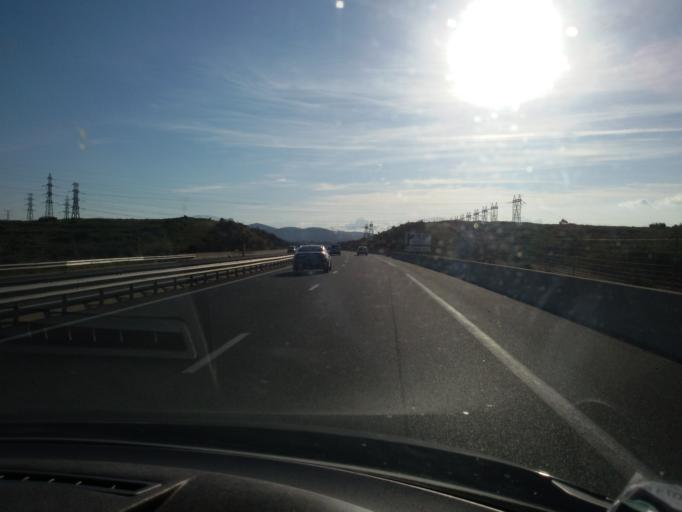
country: FR
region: Languedoc-Roussillon
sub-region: Departement de l'Herault
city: Murviel-les-Montpellier
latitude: 43.6326
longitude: 3.7255
